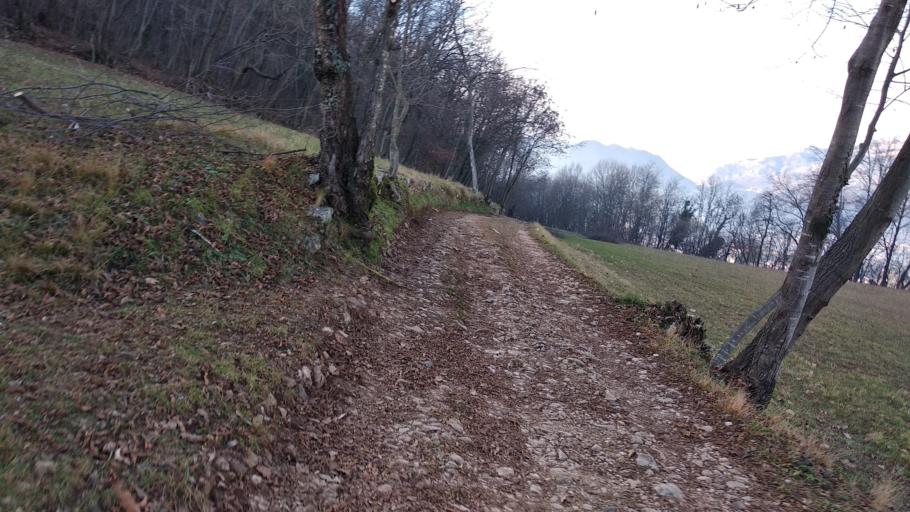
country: IT
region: Veneto
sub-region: Provincia di Vicenza
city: Schio
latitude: 45.6960
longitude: 11.3583
